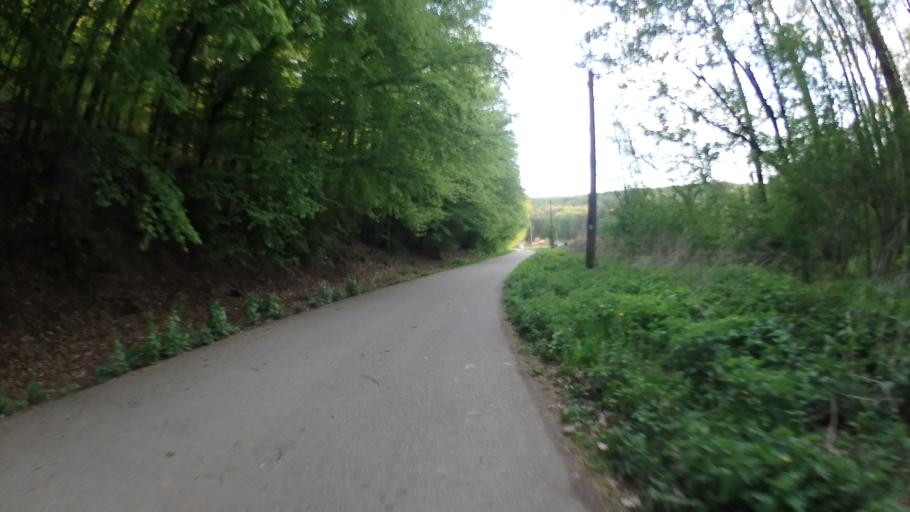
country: CZ
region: South Moravian
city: Strelice
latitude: 49.1389
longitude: 16.4777
